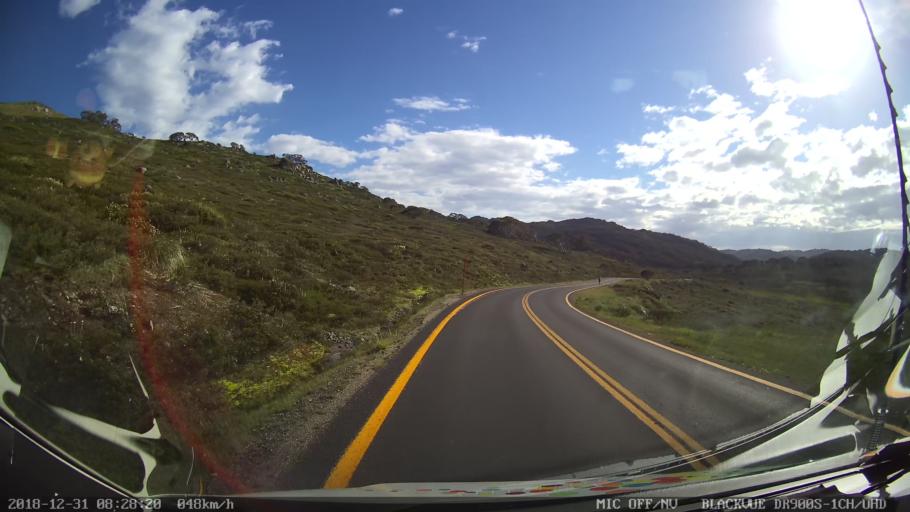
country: AU
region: New South Wales
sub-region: Snowy River
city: Jindabyne
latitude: -36.4288
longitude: 148.3448
